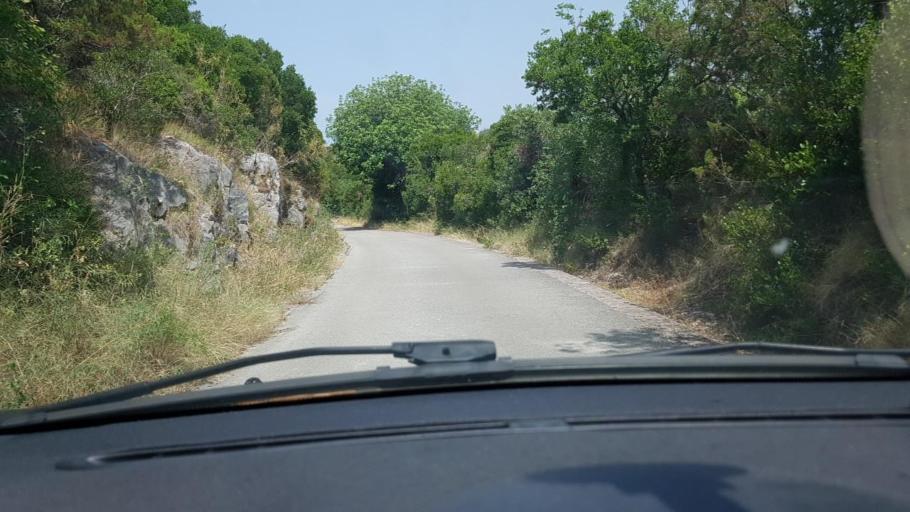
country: ME
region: Herceg Novi
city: Herceg-Novi
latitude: 42.3985
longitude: 18.5221
